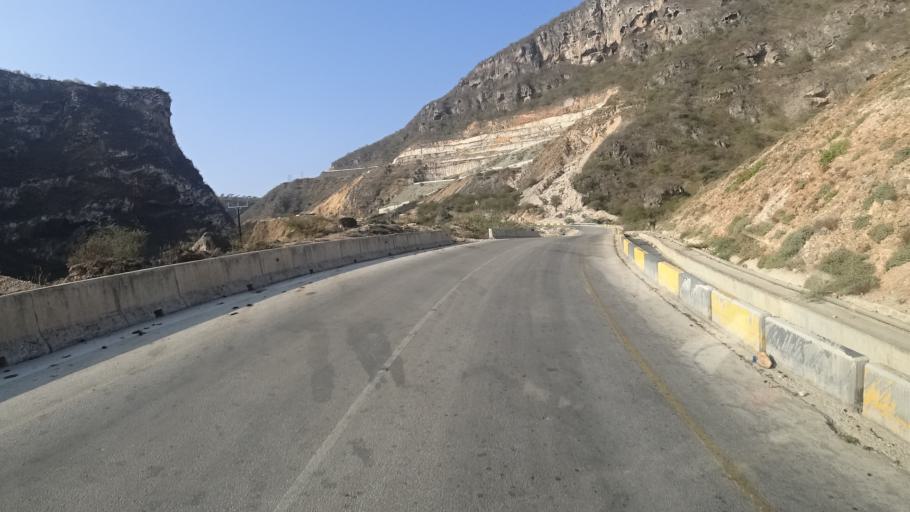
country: YE
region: Al Mahrah
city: Hawf
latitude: 16.7409
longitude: 53.2285
